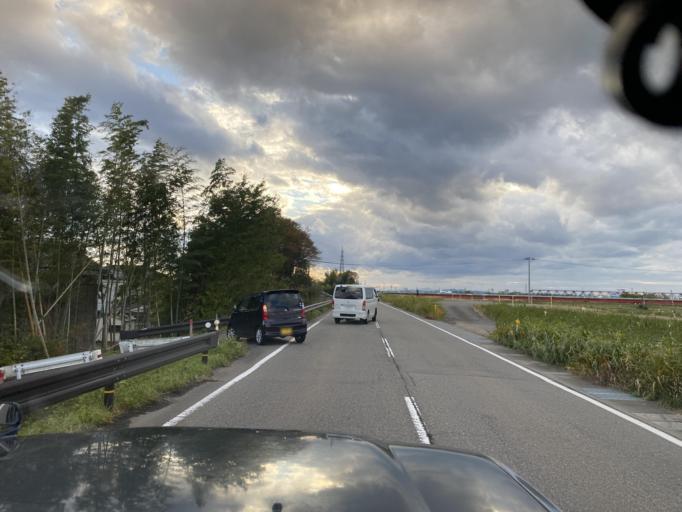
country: JP
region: Niigata
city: Sanjo
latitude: 37.6471
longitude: 138.9534
